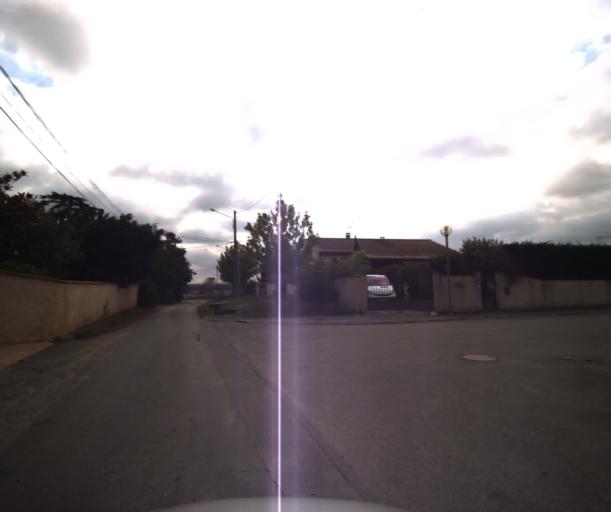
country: FR
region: Midi-Pyrenees
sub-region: Departement de la Haute-Garonne
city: Labastidette
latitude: 43.4484
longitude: 1.2915
